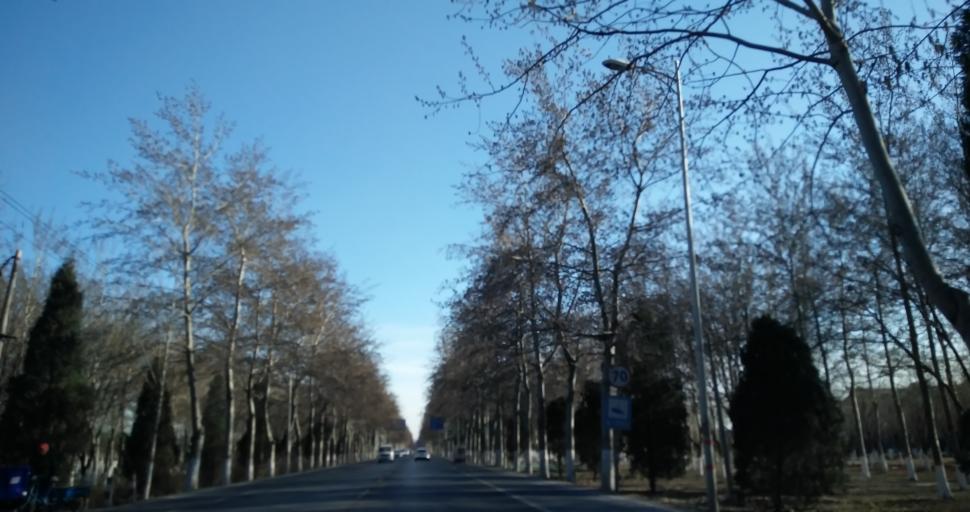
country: CN
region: Beijing
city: Yinghai
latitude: 39.7514
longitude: 116.4459
